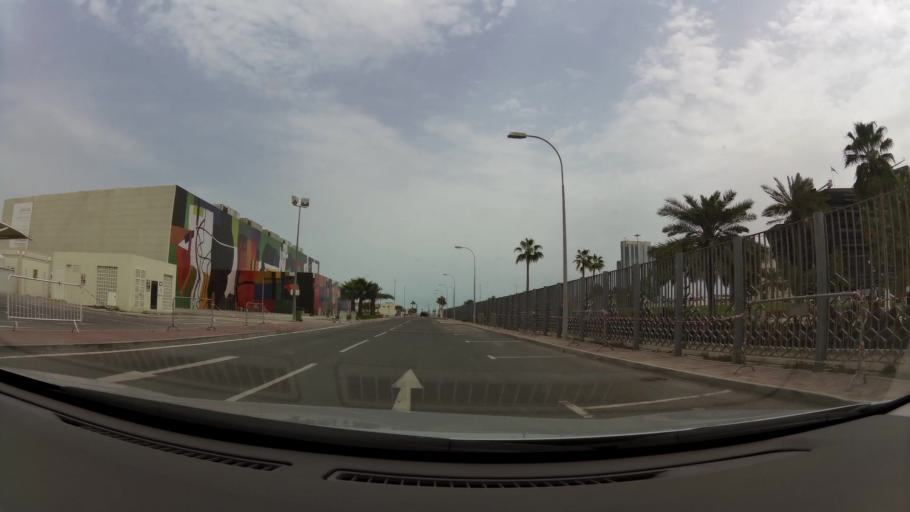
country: QA
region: Baladiyat ad Dawhah
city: Doha
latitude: 25.2926
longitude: 51.5423
